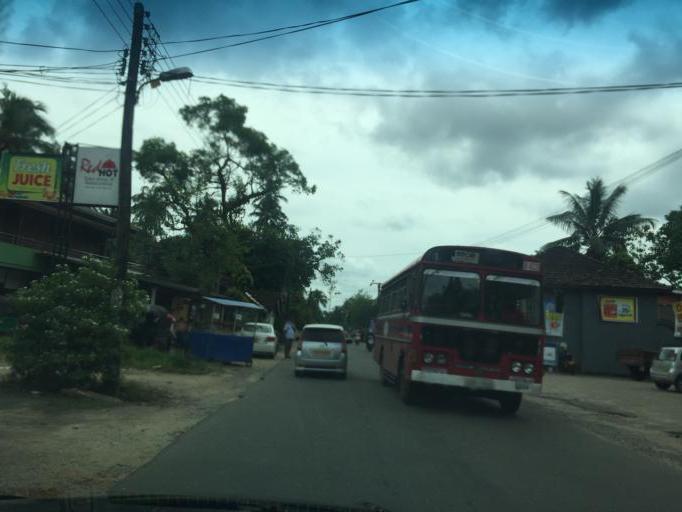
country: LK
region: Western
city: Horana South
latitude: 6.7095
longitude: 80.0664
